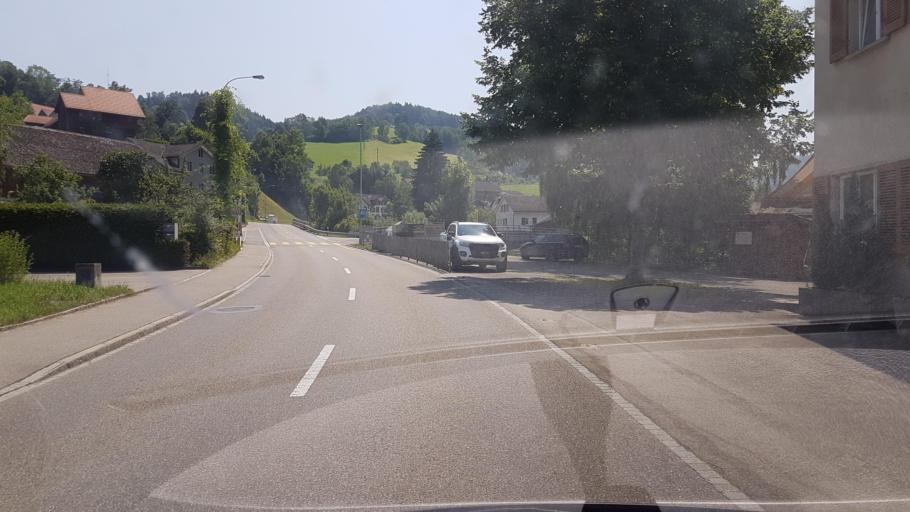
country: CH
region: Saint Gallen
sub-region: Wahlkreis Toggenburg
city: Mogelsberg
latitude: 47.3485
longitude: 9.1296
